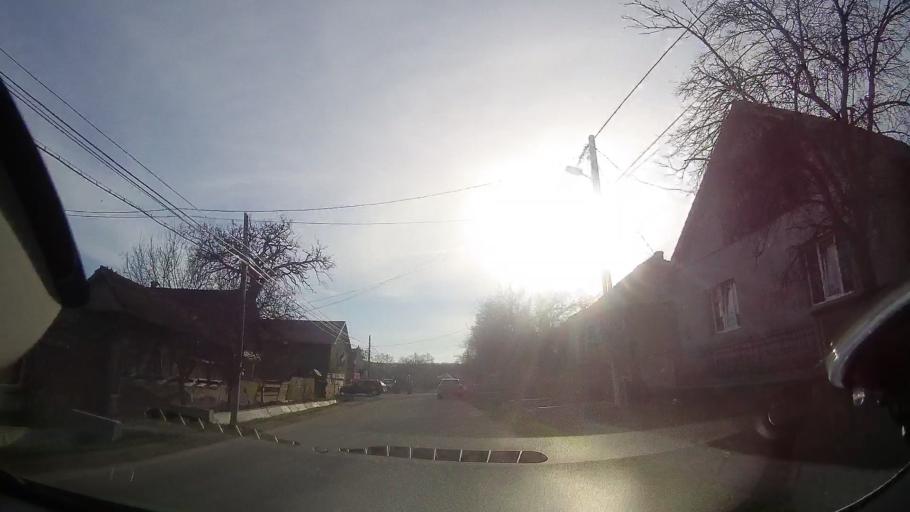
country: RO
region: Bihor
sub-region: Comuna Sarbi
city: Sarbi
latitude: 47.1941
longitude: 22.1207
